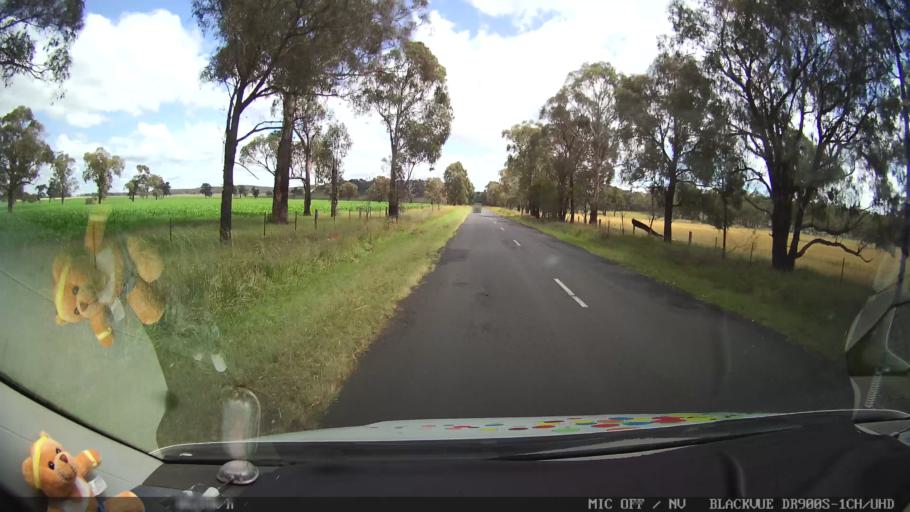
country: AU
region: New South Wales
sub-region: Glen Innes Severn
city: Glen Innes
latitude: -29.6037
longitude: 151.6667
